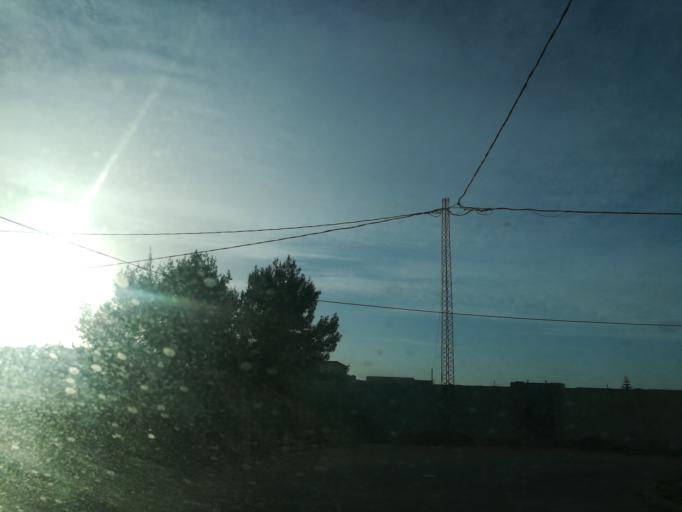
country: TN
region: Safaqis
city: Al Qarmadah
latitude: 34.8102
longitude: 10.7522
